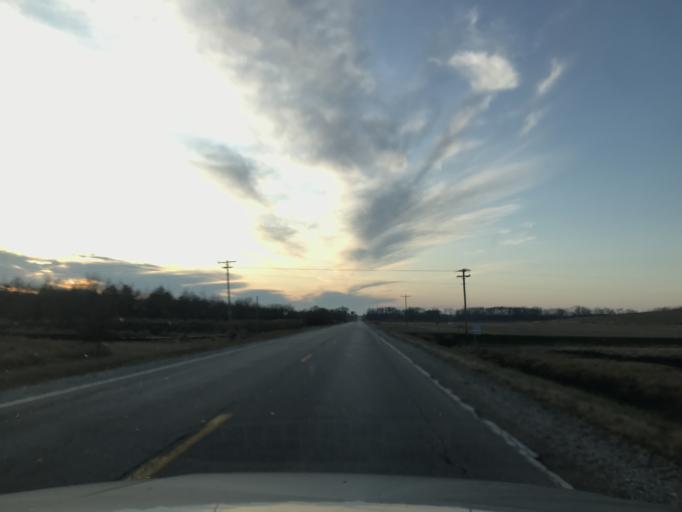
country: US
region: Illinois
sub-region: Henderson County
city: Oquawka
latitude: 41.0191
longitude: -90.8138
